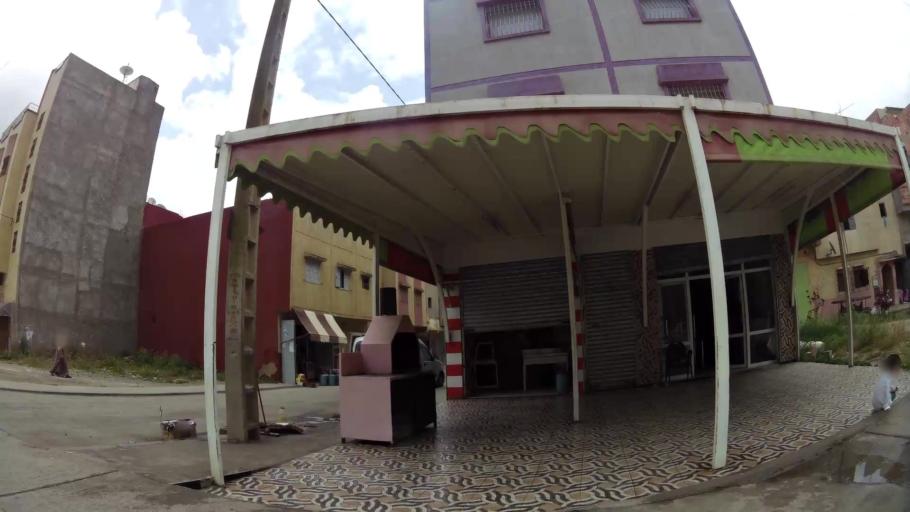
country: MA
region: Rabat-Sale-Zemmour-Zaer
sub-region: Khemisset
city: Tiflet
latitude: 33.8889
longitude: -6.3197
